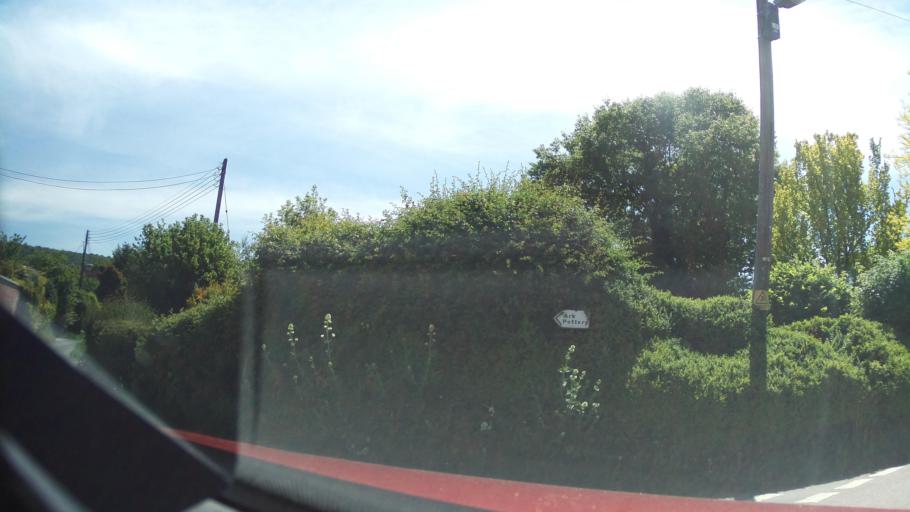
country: GB
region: England
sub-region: Devon
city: Ottery St Mary
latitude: 50.7359
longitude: -3.2753
